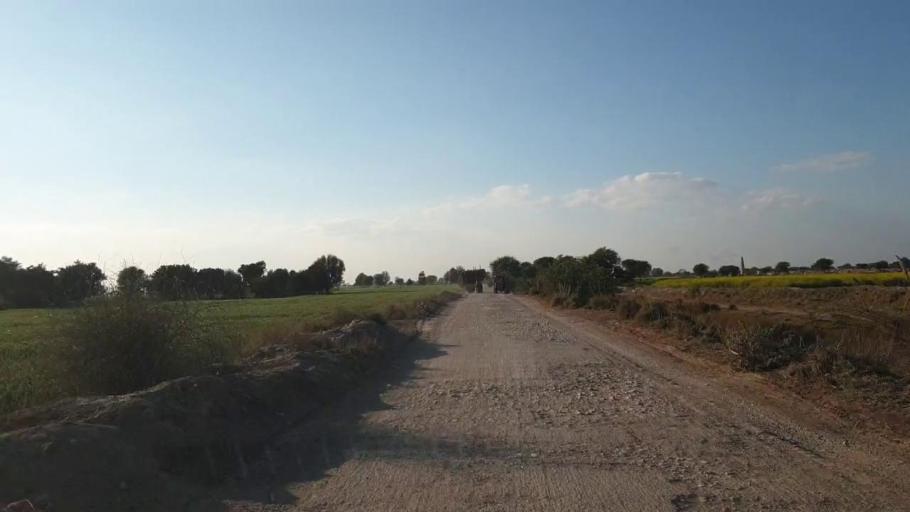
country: PK
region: Sindh
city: Shahpur Chakar
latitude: 26.1364
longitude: 68.5595
